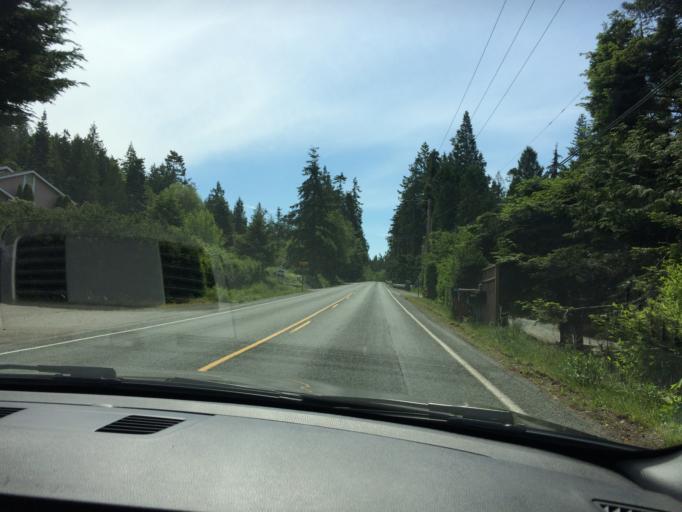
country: US
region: Washington
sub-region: Skagit County
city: Anacortes
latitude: 48.4708
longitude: -122.6540
